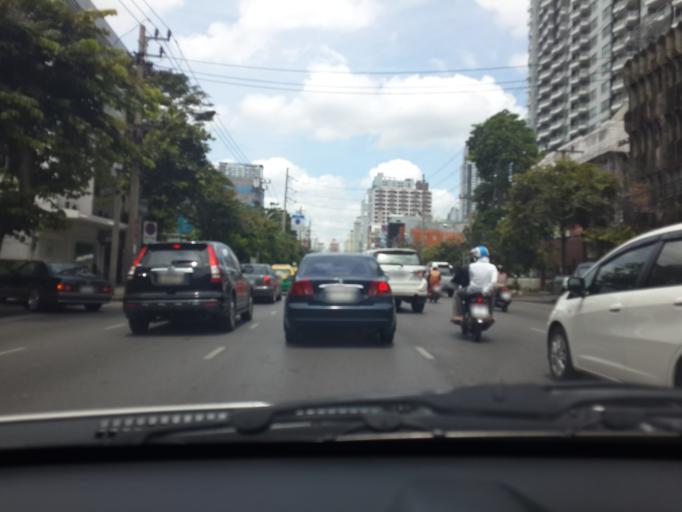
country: TH
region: Bangkok
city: Ratchathewi
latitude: 13.7555
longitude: 100.5252
